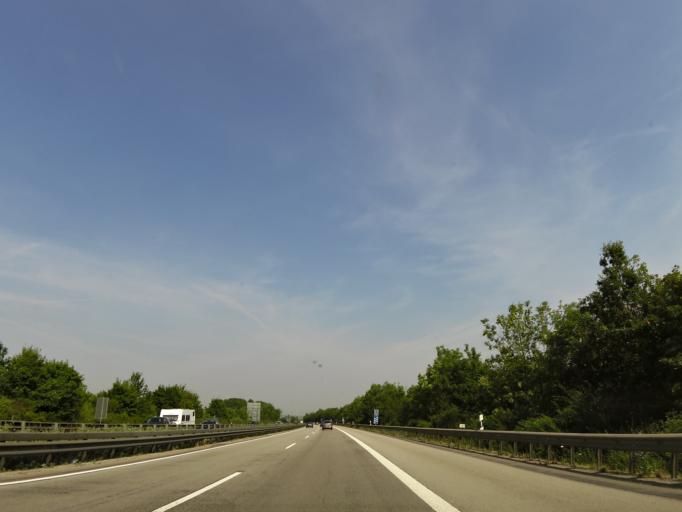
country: DE
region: Rheinland-Pfalz
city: Albig
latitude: 49.7839
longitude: 8.1037
